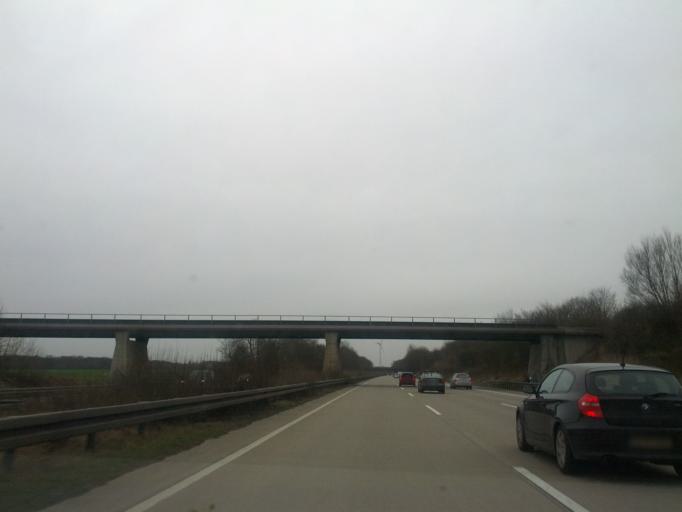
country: DE
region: Lower Saxony
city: Harsum
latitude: 52.2240
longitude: 9.9337
